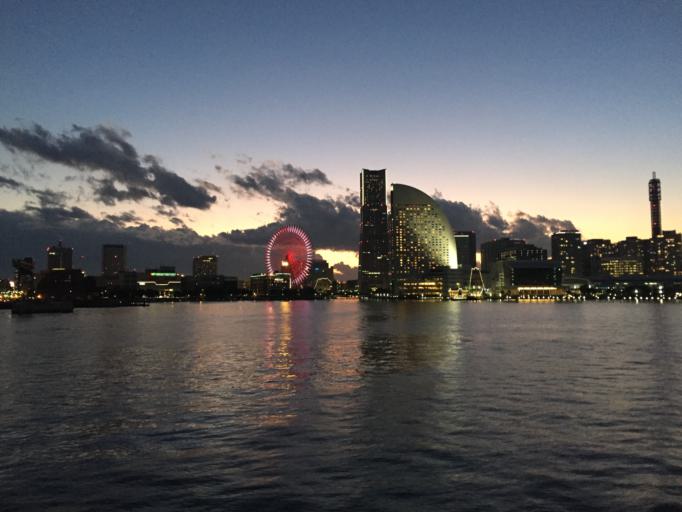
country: JP
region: Kanagawa
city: Yokohama
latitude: 35.4601
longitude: 139.6451
